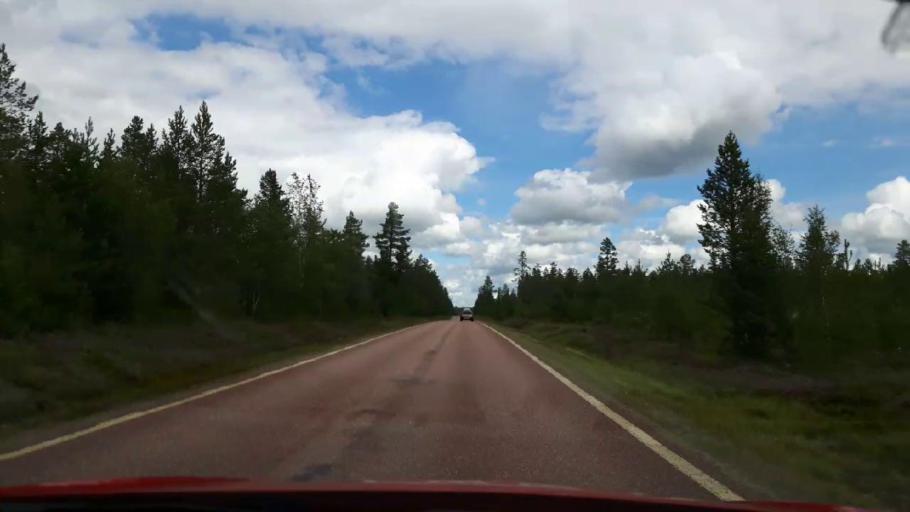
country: NO
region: Hedmark
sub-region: Trysil
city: Innbygda
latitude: 61.8829
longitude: 12.9742
